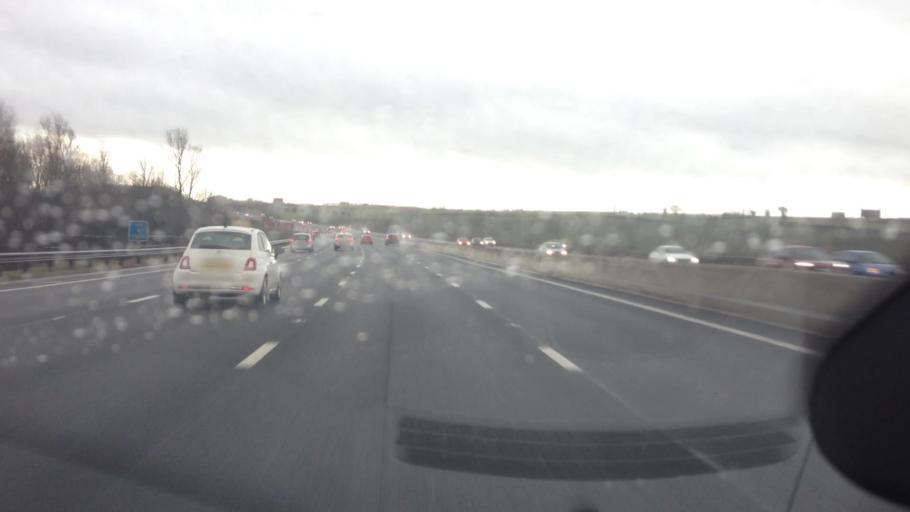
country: GB
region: England
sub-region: City and Borough of Wakefield
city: Ossett
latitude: 53.6975
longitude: -1.5572
